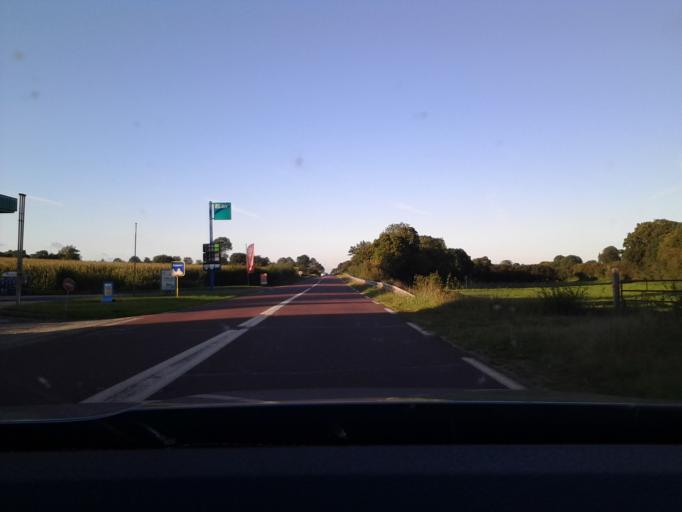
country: FR
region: Lower Normandy
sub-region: Departement de la Manche
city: Valognes
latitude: 49.4593
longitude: -1.4911
